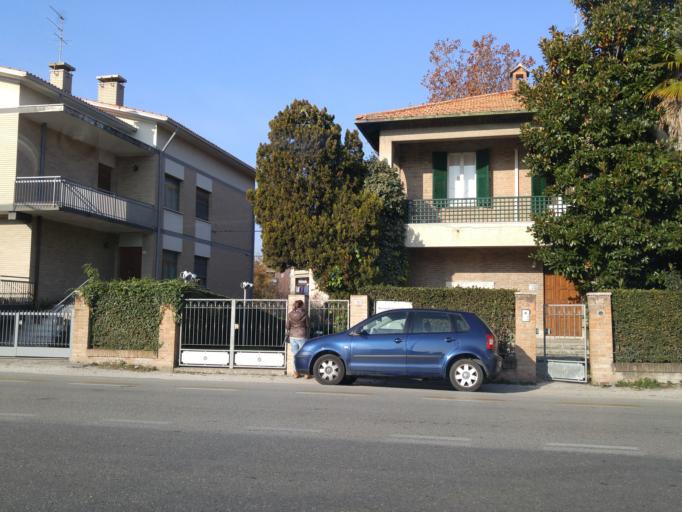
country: IT
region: The Marches
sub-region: Provincia di Pesaro e Urbino
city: Centinarola
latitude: 43.8341
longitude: 13.0037
